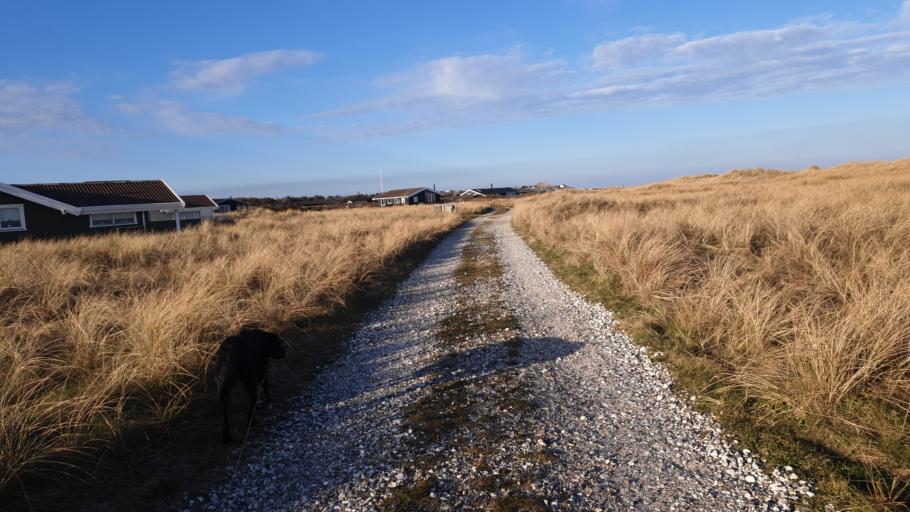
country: DK
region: North Denmark
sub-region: Hjorring Kommune
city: Hjorring
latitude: 57.4912
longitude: 9.8244
